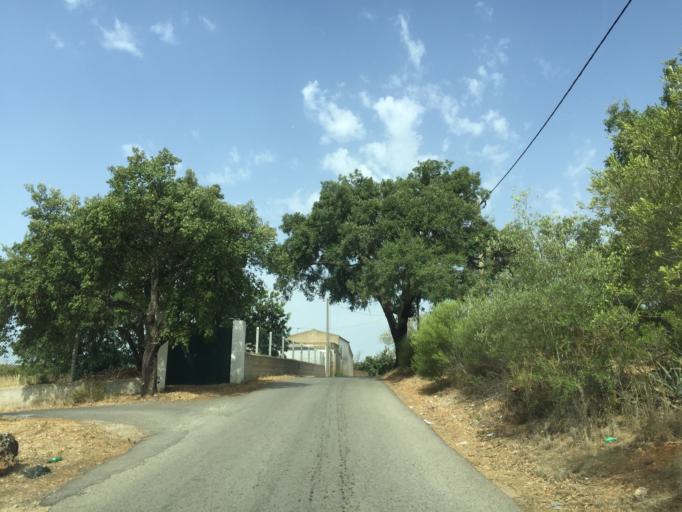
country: PT
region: Faro
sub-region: Loule
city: Vilamoura
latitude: 37.1024
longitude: -8.0975
